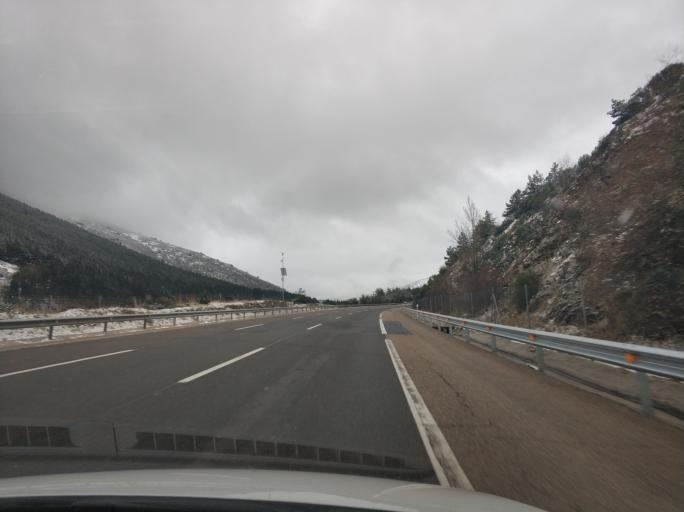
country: ES
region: Madrid
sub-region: Provincia de Madrid
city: Somosierra
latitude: 41.1699
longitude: -3.5823
